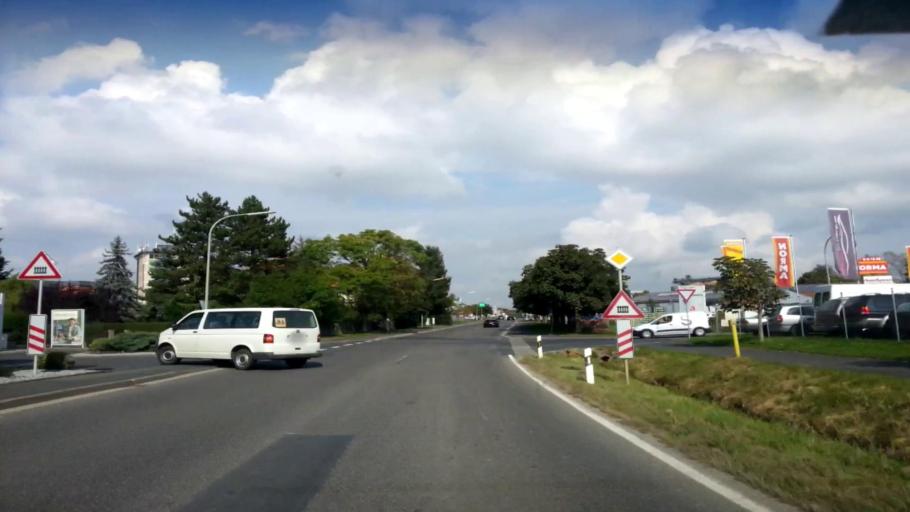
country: DE
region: Bavaria
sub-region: Regierungsbezirk Unterfranken
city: Wiesentheid
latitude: 49.7863
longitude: 10.3406
